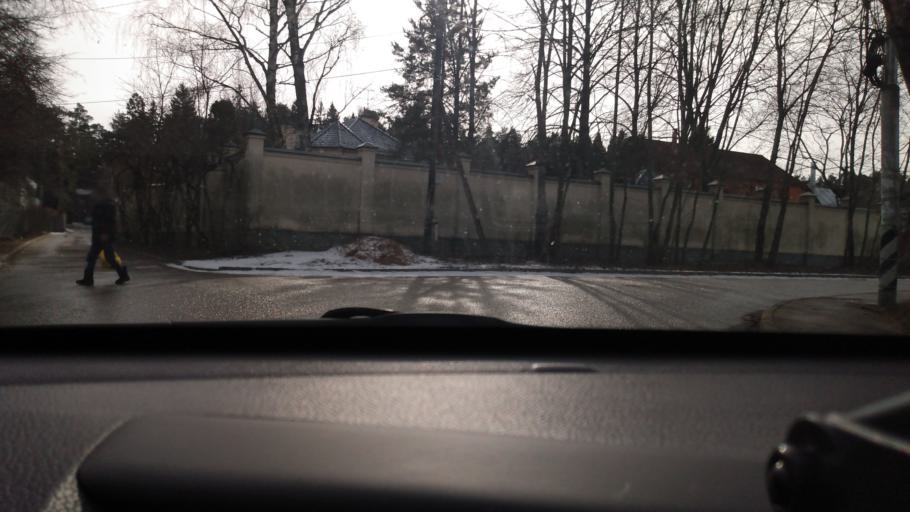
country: RU
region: Moskovskaya
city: Barvikha
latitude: 55.7335
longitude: 37.2507
